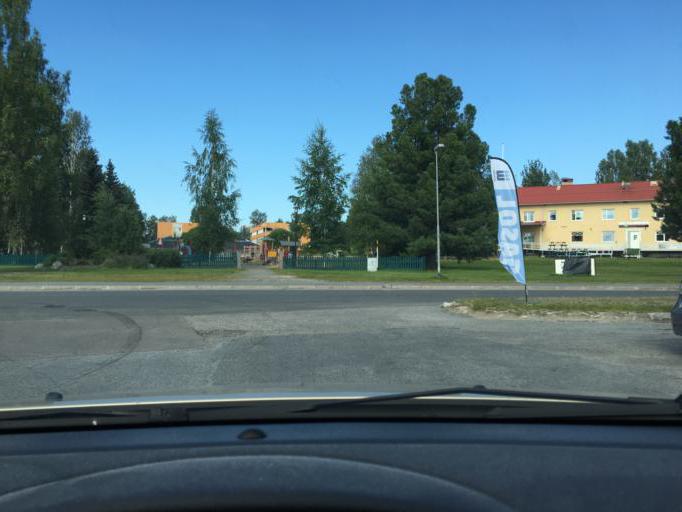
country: SE
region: Norrbotten
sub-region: Bodens Kommun
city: Boden
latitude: 65.8260
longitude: 21.7149
